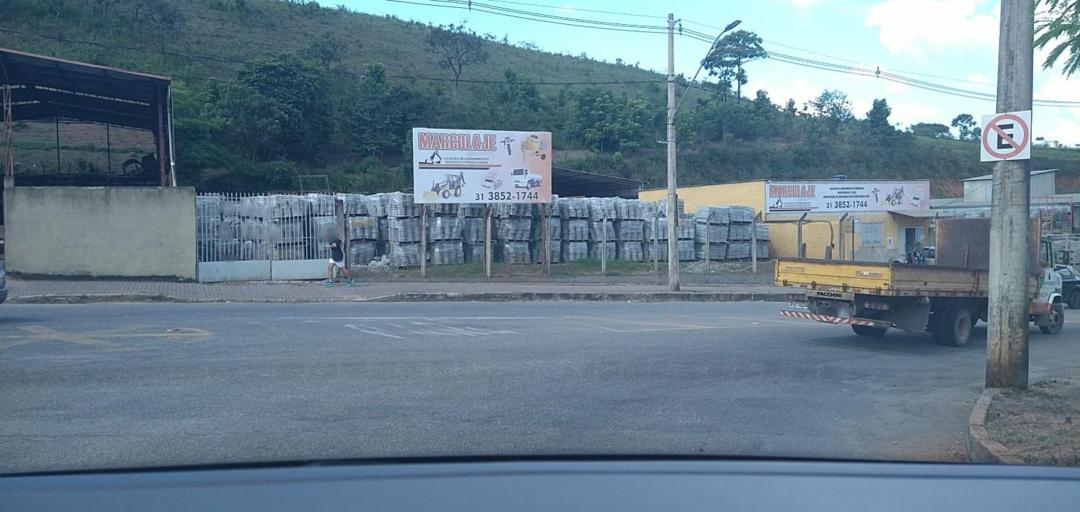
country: BR
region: Minas Gerais
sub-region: Joao Monlevade
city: Joao Monlevade
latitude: -19.8110
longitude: -43.1925
